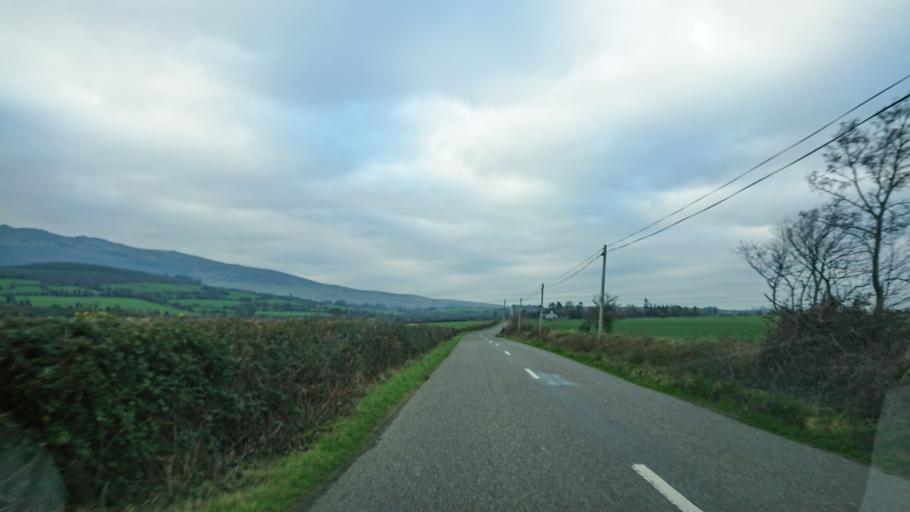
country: IE
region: Munster
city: Carrick-on-Suir
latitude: 52.3147
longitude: -7.5350
